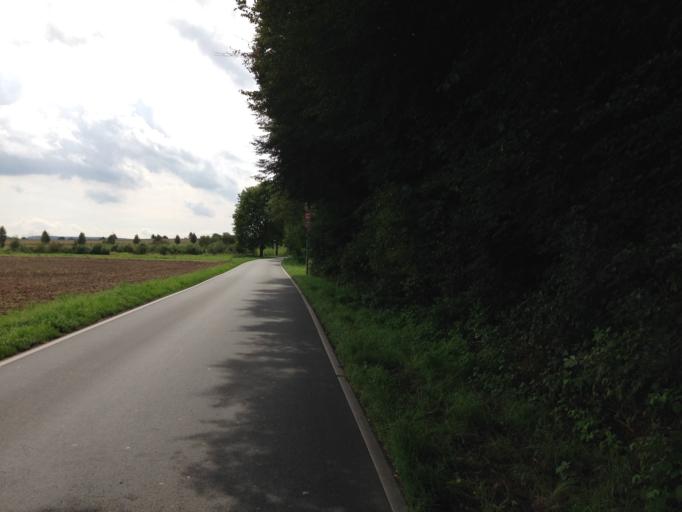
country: DE
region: Hesse
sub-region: Regierungsbezirk Giessen
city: Hoernsheim
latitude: 50.5366
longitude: 8.6604
